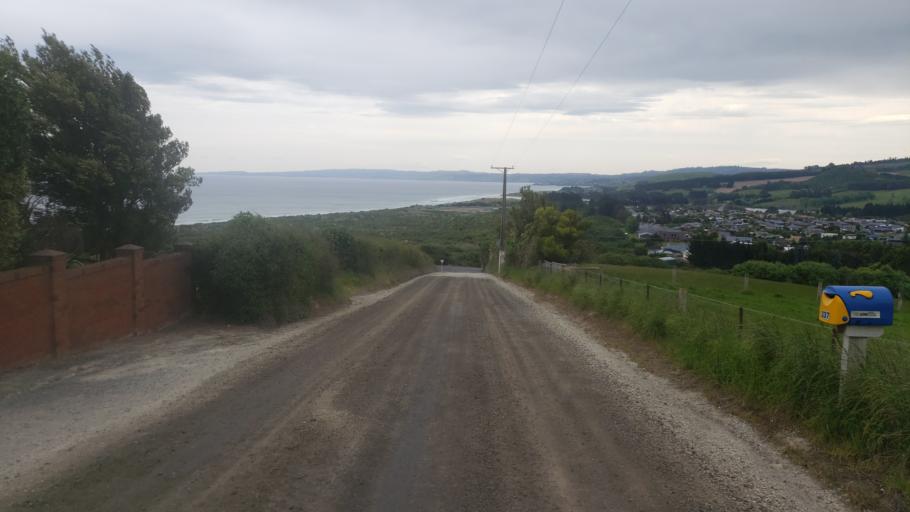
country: NZ
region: Otago
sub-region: Dunedin City
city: Dunedin
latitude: -45.9222
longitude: 170.4188
